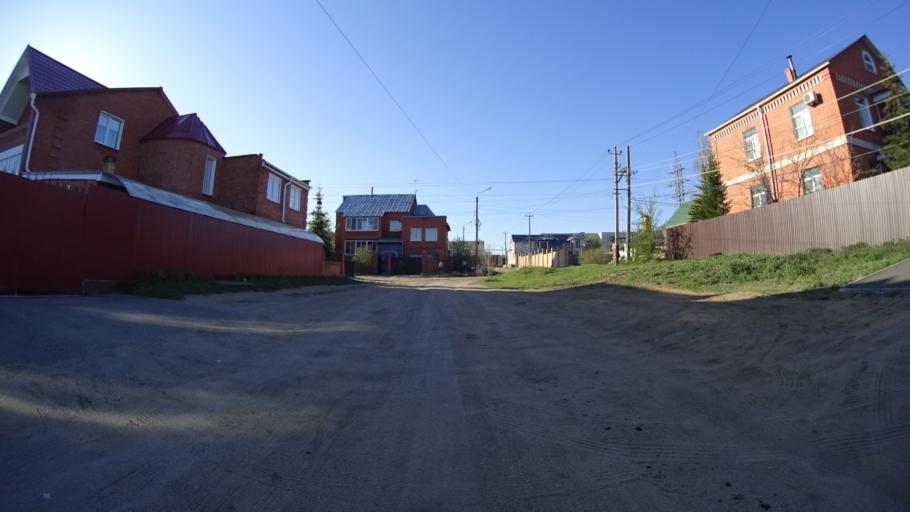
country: RU
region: Chelyabinsk
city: Troitsk
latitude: 54.0698
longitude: 61.5342
